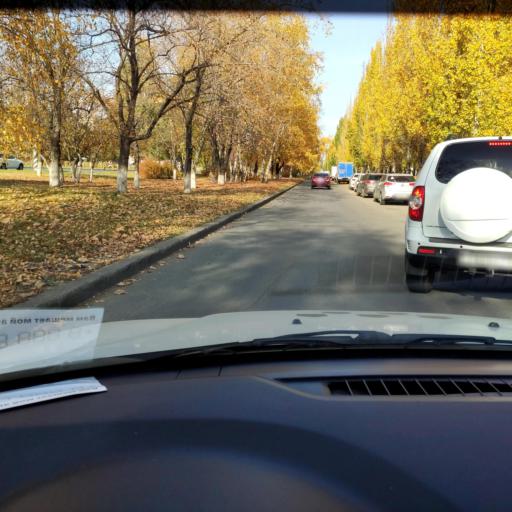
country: RU
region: Samara
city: Tol'yatti
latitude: 53.5308
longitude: 49.2984
